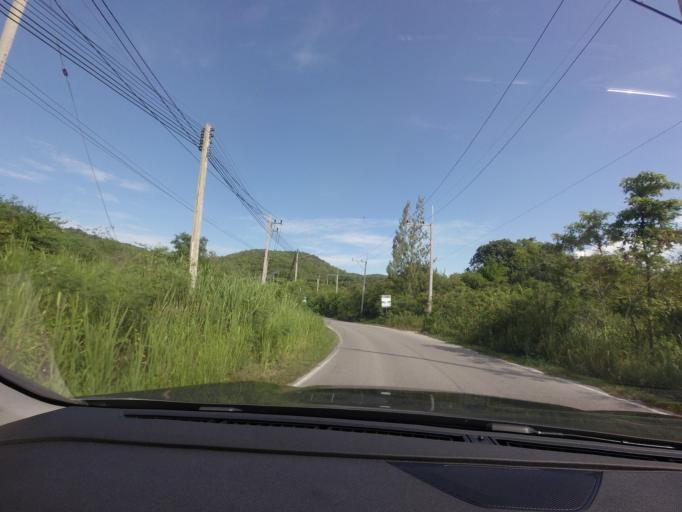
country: TH
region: Prachuap Khiri Khan
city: Hua Hin
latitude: 12.4967
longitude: 99.9396
